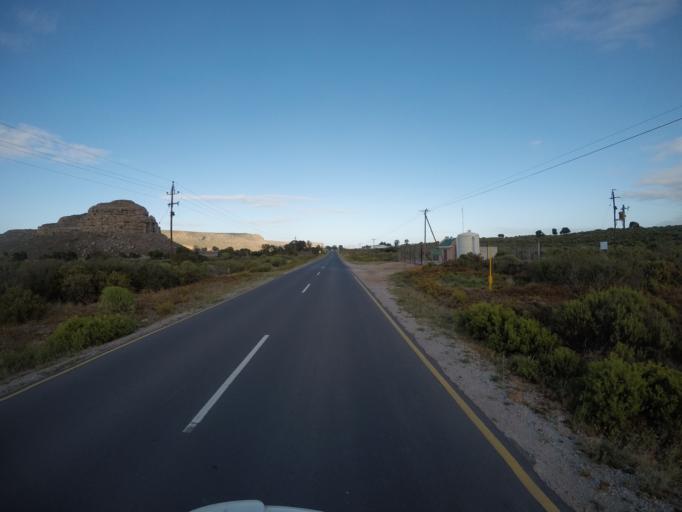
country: ZA
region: Western Cape
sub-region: West Coast District Municipality
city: Clanwilliam
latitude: -32.3130
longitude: 18.3607
